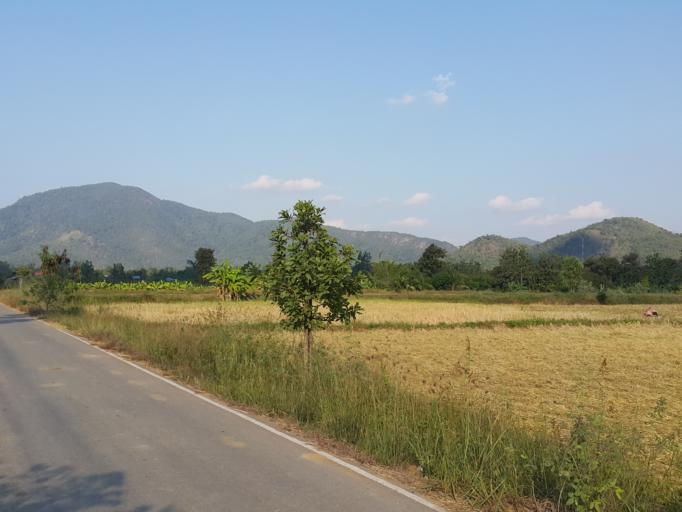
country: TH
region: Sukhothai
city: Thung Saliam
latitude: 17.3386
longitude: 99.4401
